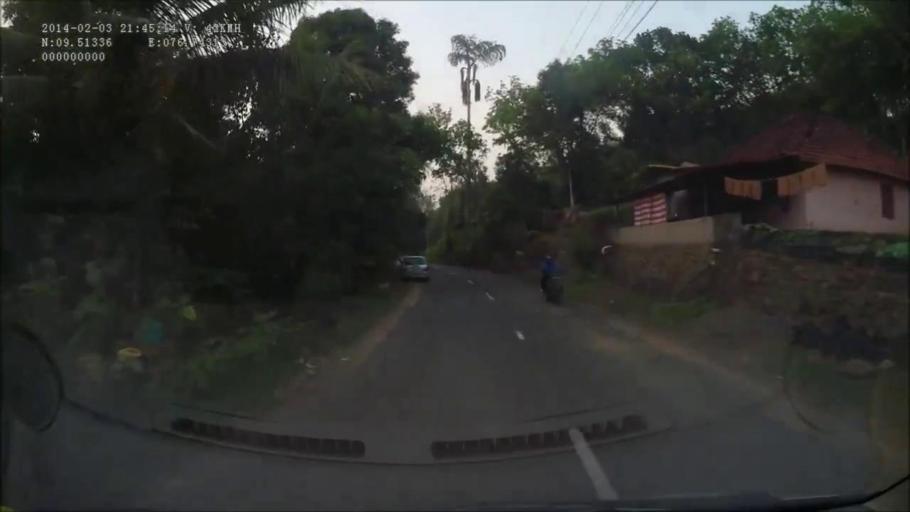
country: IN
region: Kerala
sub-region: Kottayam
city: Erattupetta
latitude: 9.5145
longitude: 76.7425
